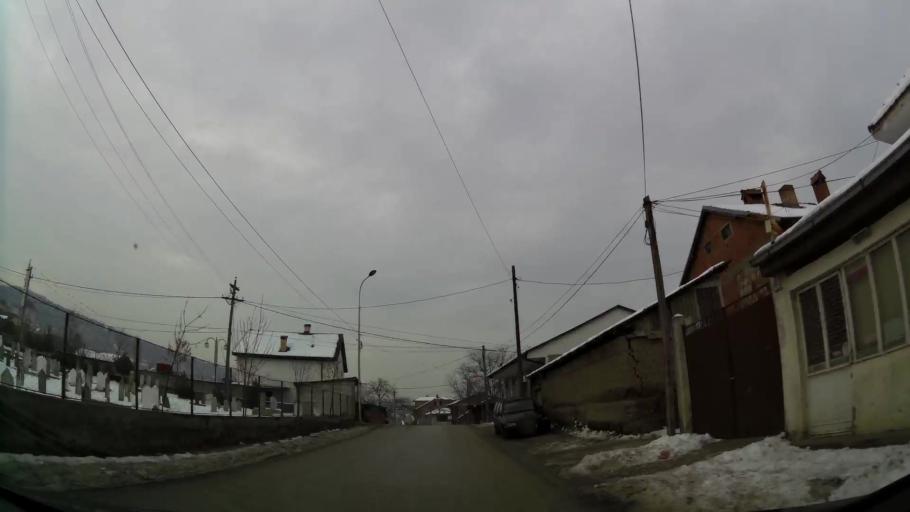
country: MK
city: Kondovo
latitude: 42.0111
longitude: 21.3123
